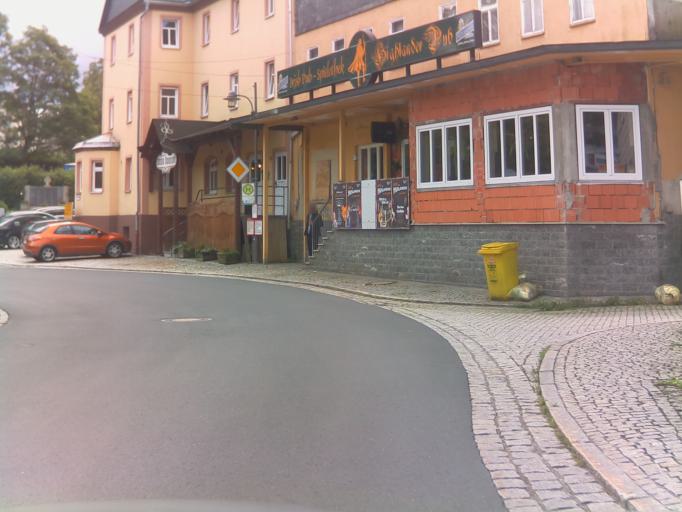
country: DE
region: Bavaria
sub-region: Upper Franconia
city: Tettau
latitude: 50.4694
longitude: 11.2580
